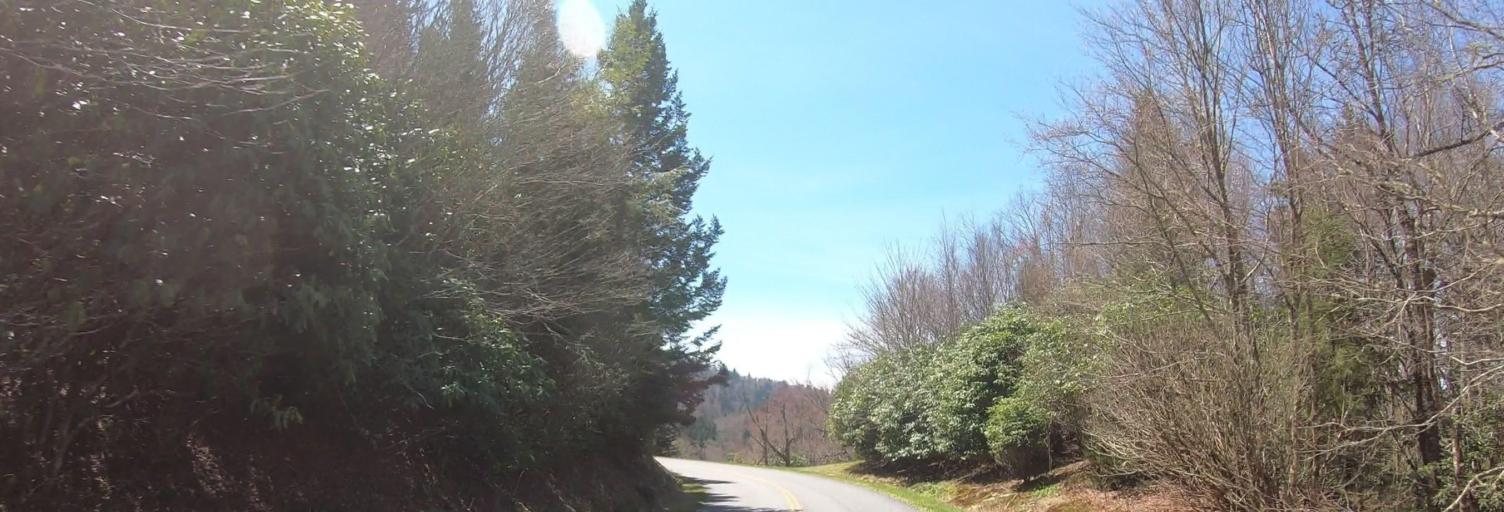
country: US
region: North Carolina
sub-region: Haywood County
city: Maggie Valley
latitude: 35.4734
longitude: -83.1411
